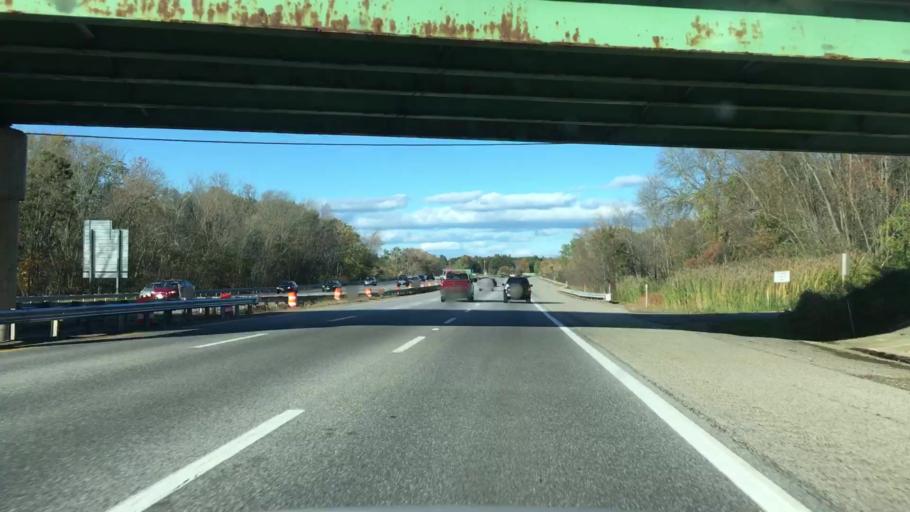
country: US
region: Maine
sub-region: York County
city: Biddeford
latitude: 43.4959
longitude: -70.4900
